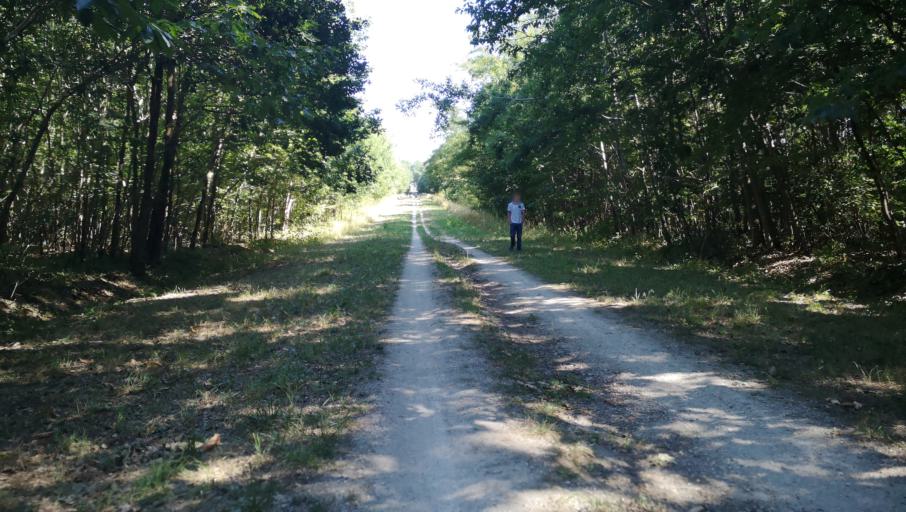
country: FR
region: Centre
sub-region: Departement du Loiret
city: Saint-Jean-de-Braye
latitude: 47.9330
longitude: 1.9830
